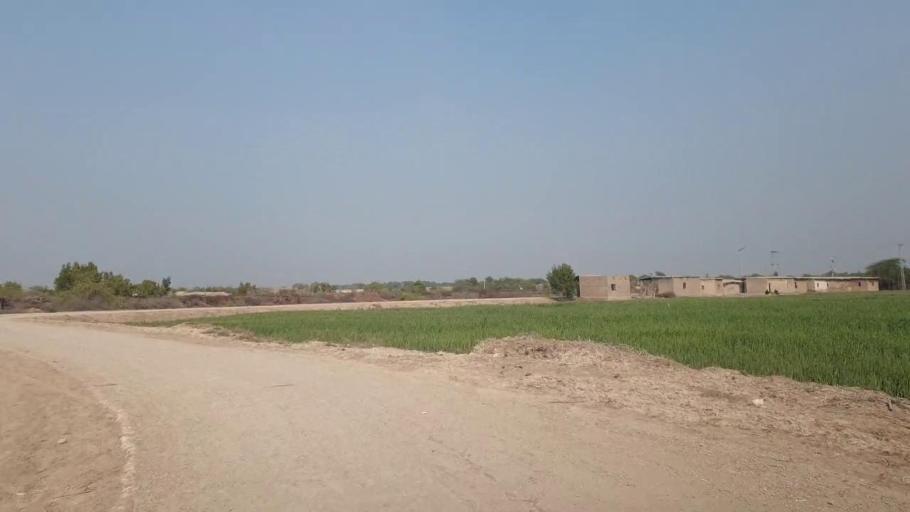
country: PK
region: Sindh
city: Mirwah Gorchani
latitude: 25.3507
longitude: 68.9484
